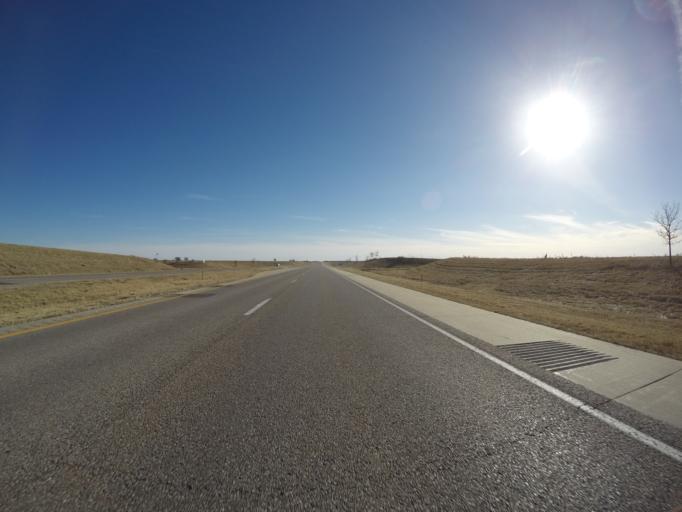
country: US
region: Nebraska
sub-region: Gage County
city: Beatrice
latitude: 40.4518
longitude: -96.7422
